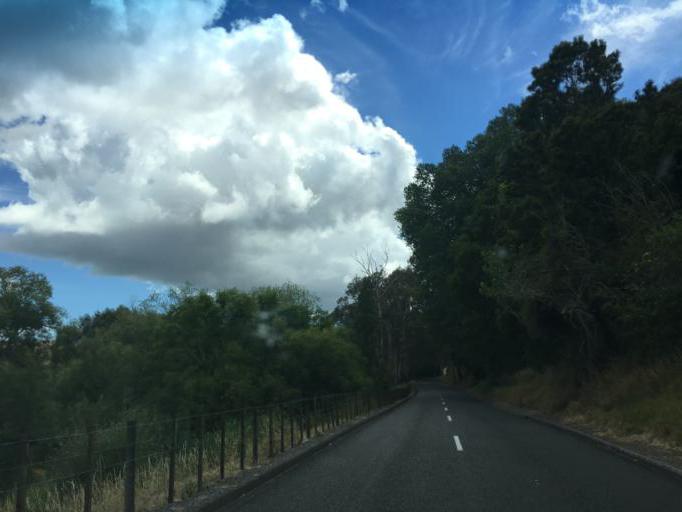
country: NZ
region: Hawke's Bay
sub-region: Hastings District
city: Hastings
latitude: -39.7232
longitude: 176.9237
